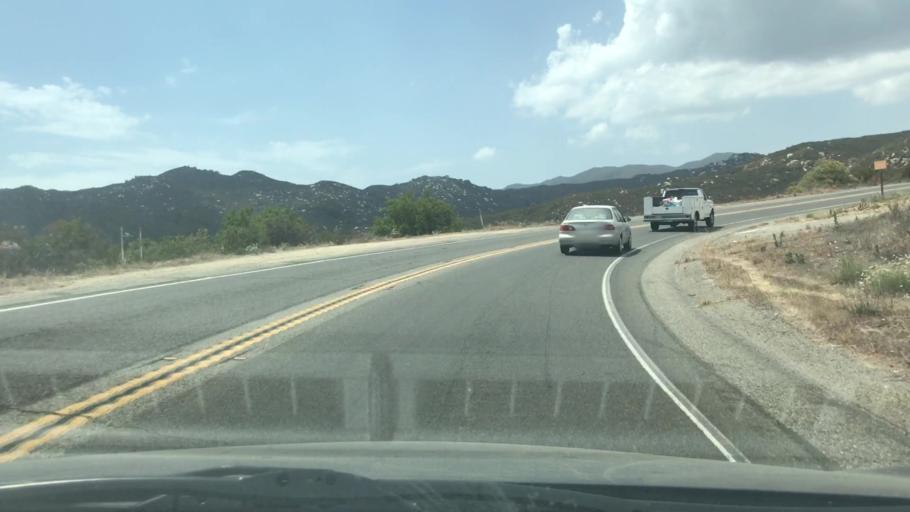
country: US
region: California
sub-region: Riverside County
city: Lakeland Village
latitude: 33.6185
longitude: -117.4267
